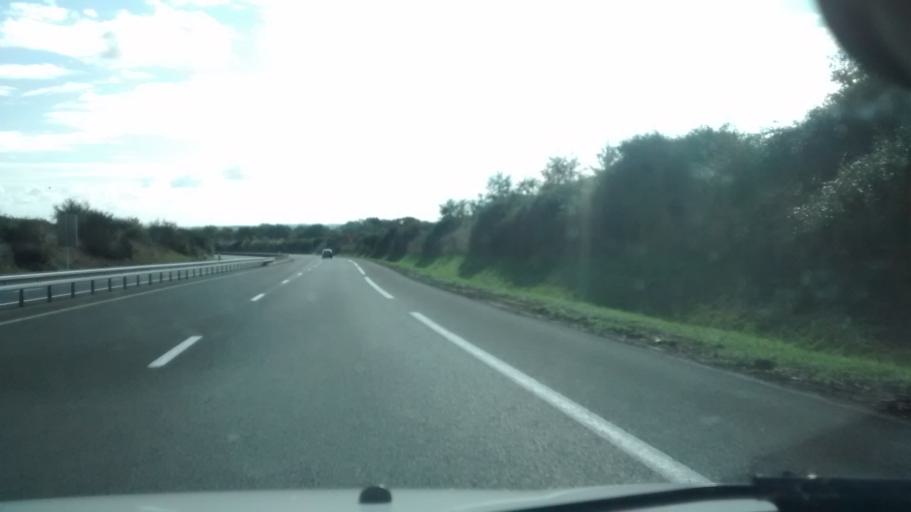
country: FR
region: Pays de la Loire
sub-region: Departement de Maine-et-Loire
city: Combree
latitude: 47.7113
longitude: -1.0042
